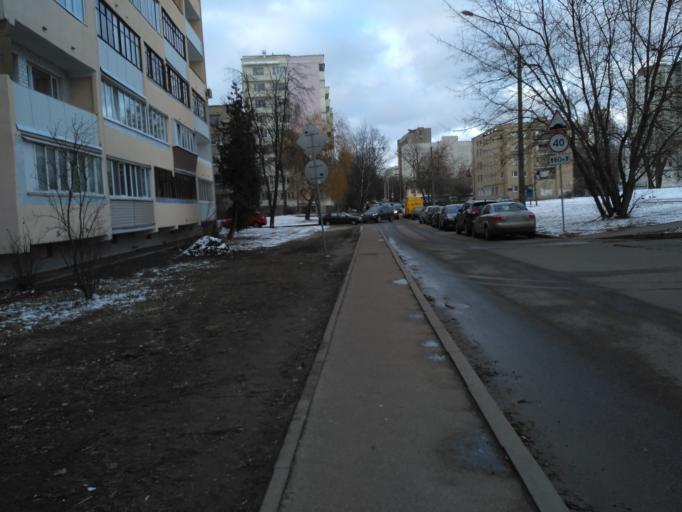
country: BY
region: Minsk
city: Minsk
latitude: 53.9237
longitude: 27.5835
